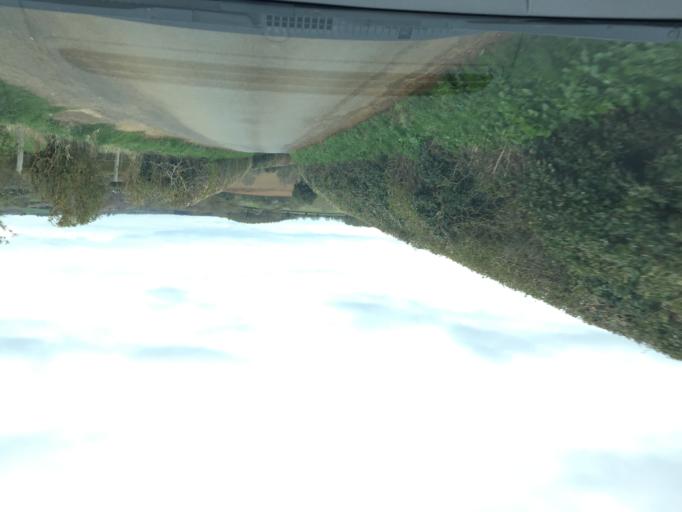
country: GB
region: England
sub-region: Oxfordshire
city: Hanwell
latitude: 52.0868
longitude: -1.3792
